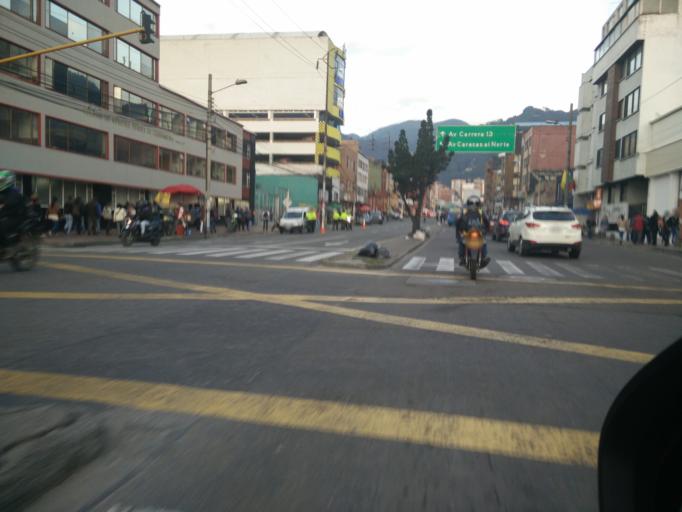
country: CO
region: Bogota D.C.
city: Bogota
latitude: 4.6500
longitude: -74.0669
